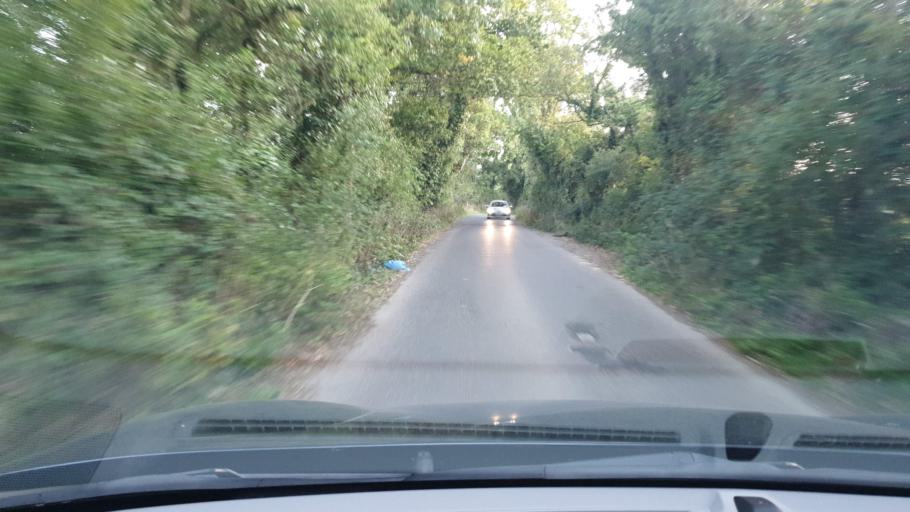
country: IE
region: Leinster
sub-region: An Mhi
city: Stamullin
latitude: 53.5925
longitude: -6.2450
